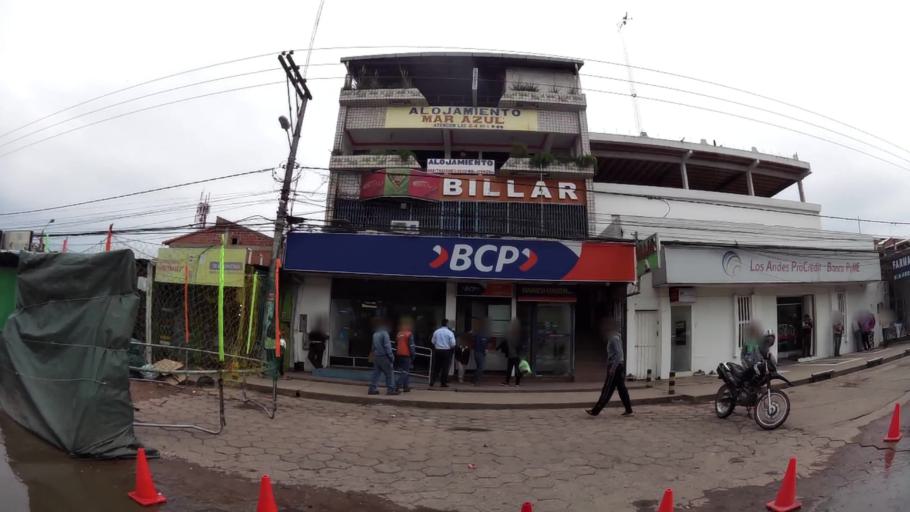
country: BO
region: Santa Cruz
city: Santa Cruz de la Sierra
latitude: -17.7640
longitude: -63.1617
